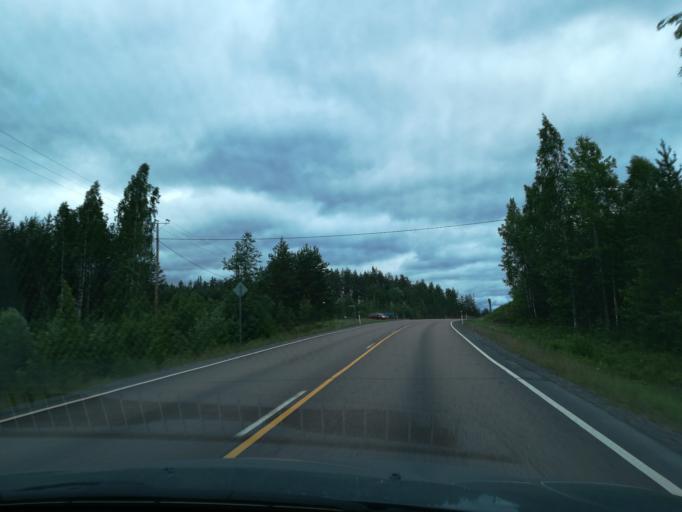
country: FI
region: Southern Savonia
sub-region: Mikkeli
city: Ristiina
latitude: 61.3452
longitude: 27.3743
